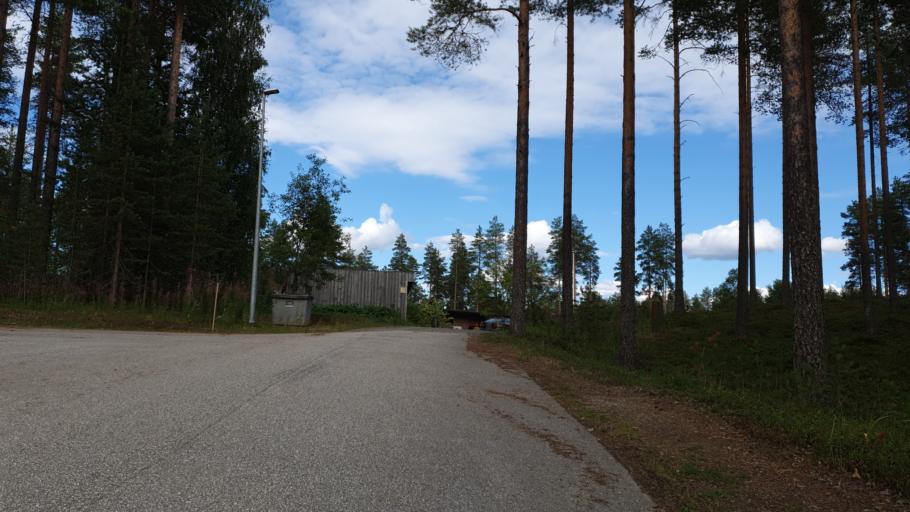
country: FI
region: Kainuu
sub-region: Kehys-Kainuu
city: Kuhmo
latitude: 64.1261
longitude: 29.5570
